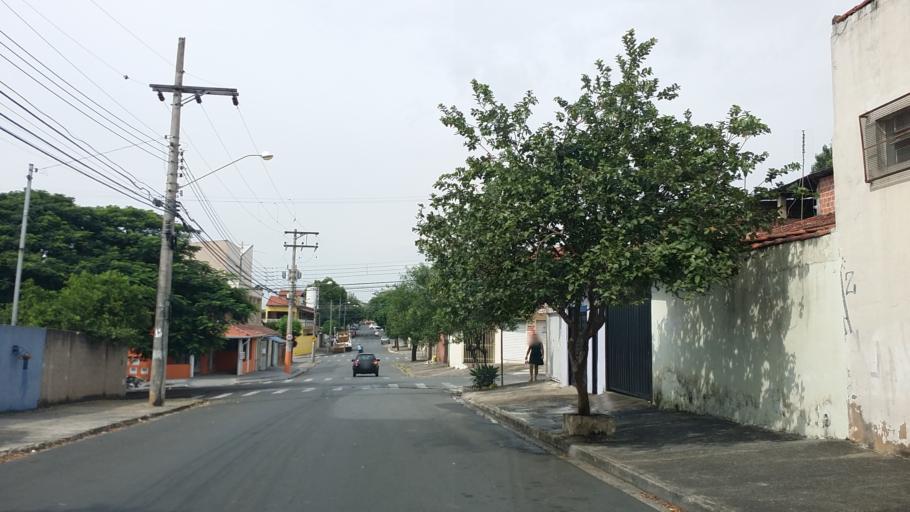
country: BR
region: Sao Paulo
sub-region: Indaiatuba
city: Indaiatuba
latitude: -23.1206
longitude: -47.2367
